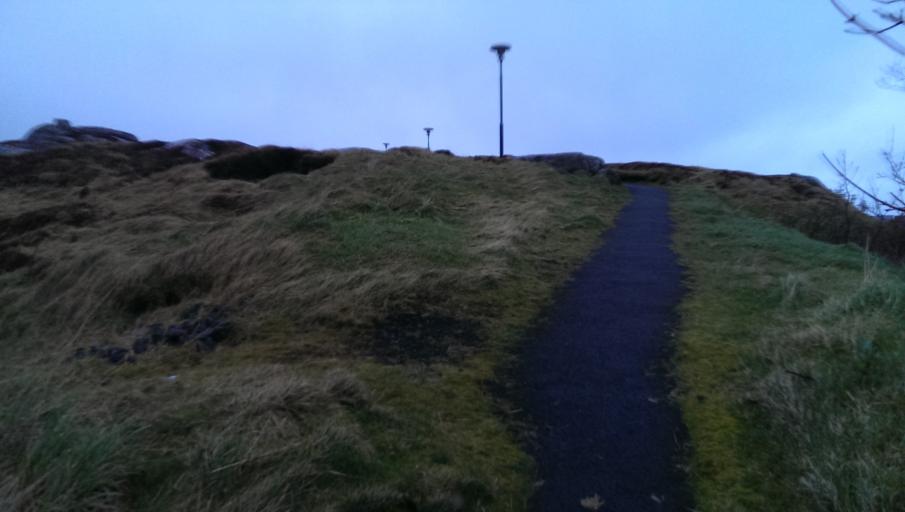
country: FO
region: Streymoy
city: Hoyvik
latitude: 62.0306
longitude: -6.7856
